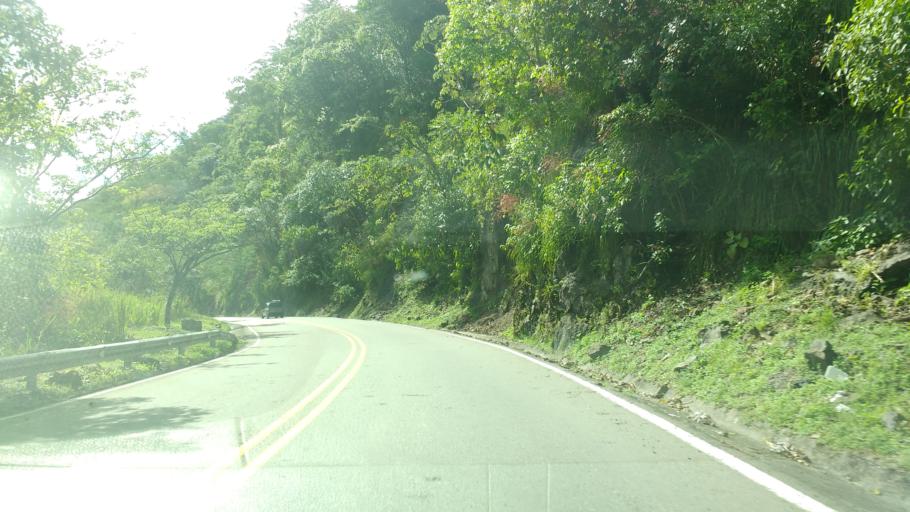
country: CO
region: Antioquia
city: Titiribi
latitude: 6.0050
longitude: -75.7960
